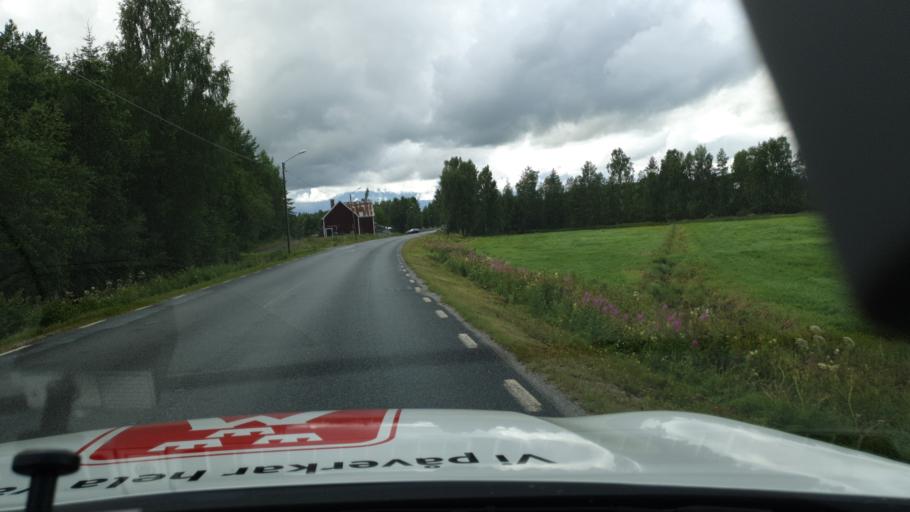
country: SE
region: Vaesterbotten
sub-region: Skelleftea Kommun
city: Viken
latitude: 64.5848
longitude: 20.9575
